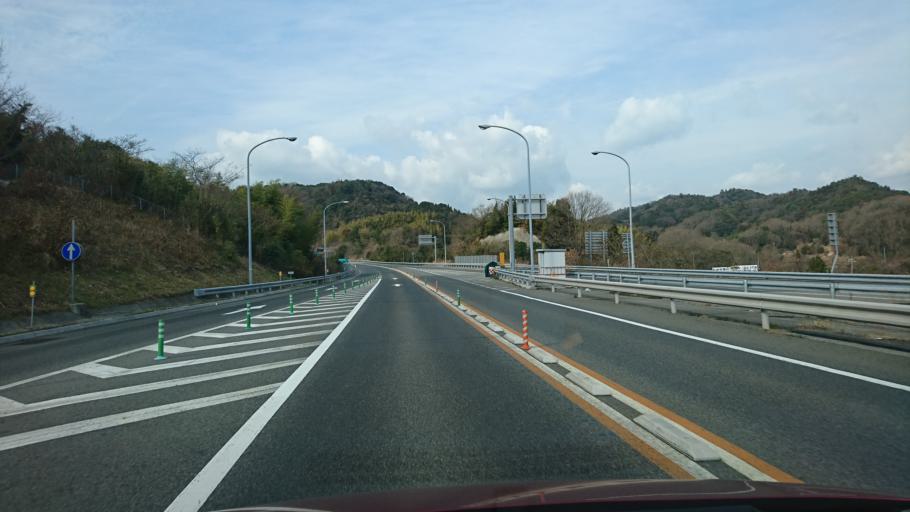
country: JP
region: Hiroshima
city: Innoshima
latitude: 34.1297
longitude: 133.0321
